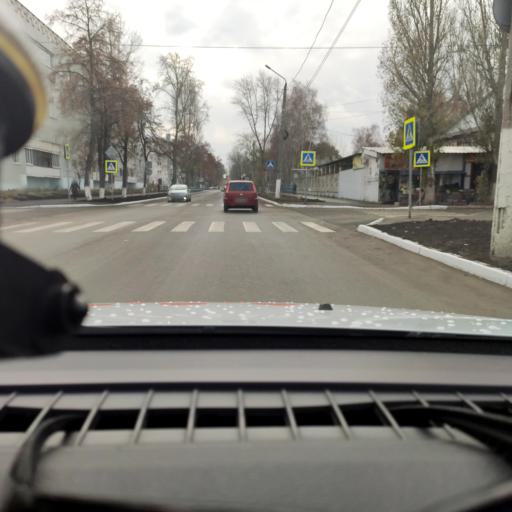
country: RU
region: Samara
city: Chapayevsk
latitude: 52.9853
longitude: 49.7206
